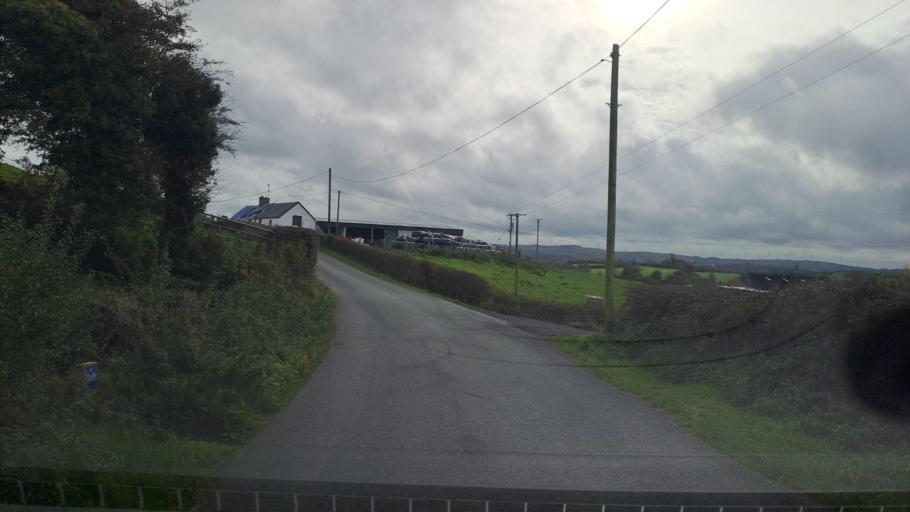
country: IE
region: Ulster
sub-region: An Cabhan
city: Bailieborough
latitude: 54.0150
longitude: -6.8989
